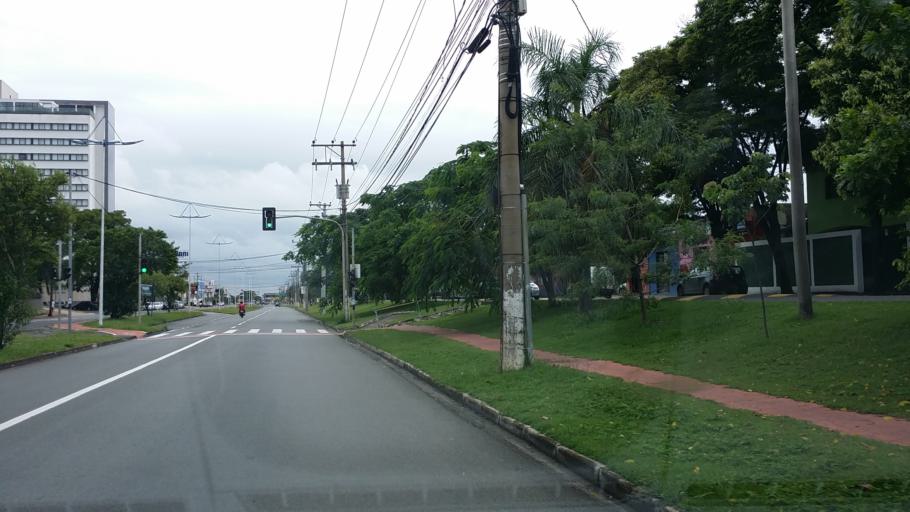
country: BR
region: Sao Paulo
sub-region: Indaiatuba
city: Indaiatuba
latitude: -23.1151
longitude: -47.2220
